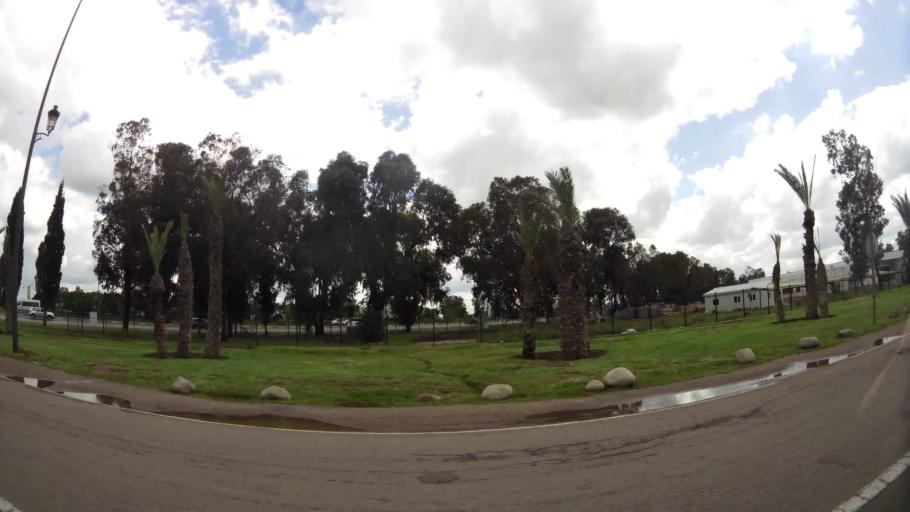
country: MA
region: Chaouia-Ouardigha
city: Nouaseur
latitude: 33.3822
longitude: -7.5660
